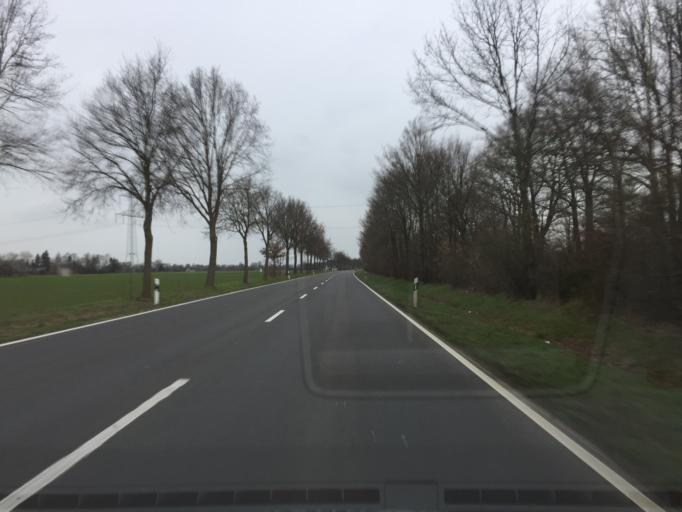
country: DE
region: North Rhine-Westphalia
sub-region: Regierungsbezirk Detmold
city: Petershagen
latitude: 52.3999
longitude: 8.9545
